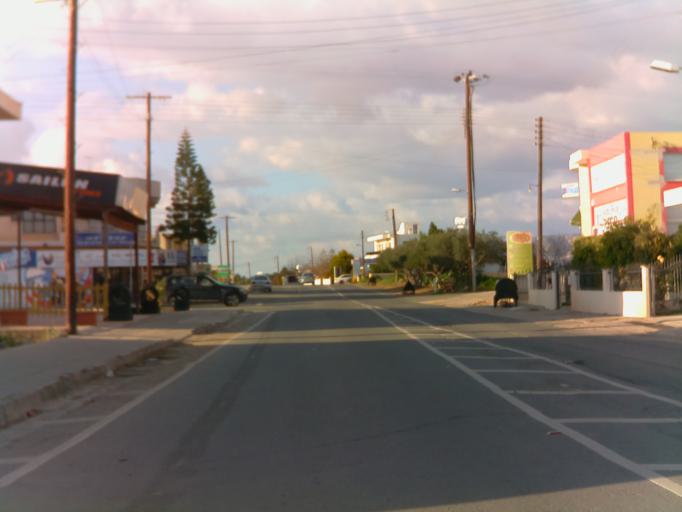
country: CY
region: Pafos
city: Chlorakas
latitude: 34.8006
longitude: 32.4138
